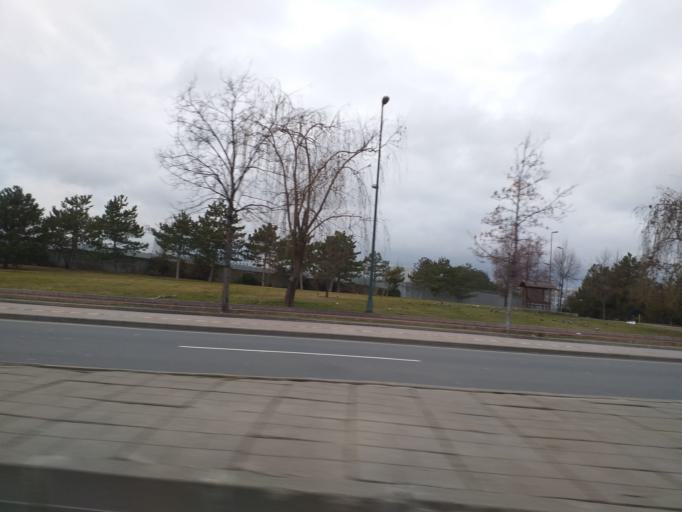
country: TR
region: Ankara
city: Ankara
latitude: 39.9692
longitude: 32.8359
